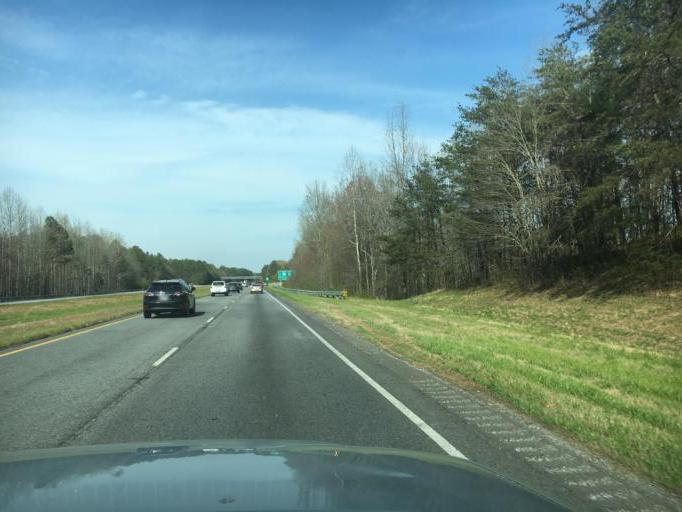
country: US
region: Georgia
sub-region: Habersham County
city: Baldwin
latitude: 34.5105
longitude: -83.5613
